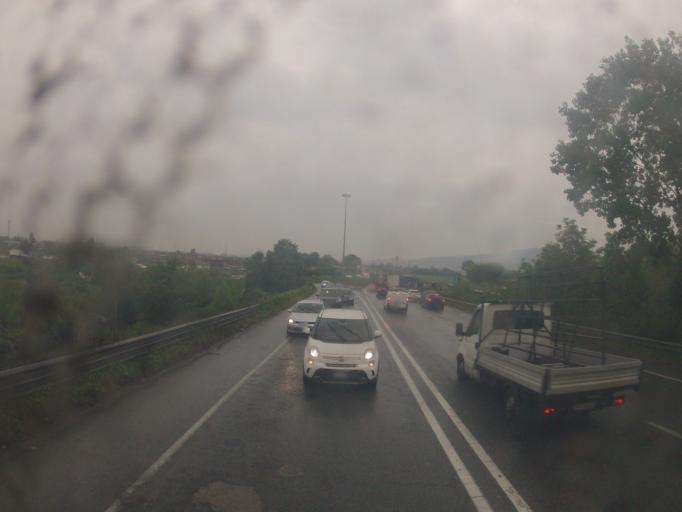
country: IT
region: Piedmont
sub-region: Provincia di Torino
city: Tagliaferro
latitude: 44.9738
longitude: 7.6697
